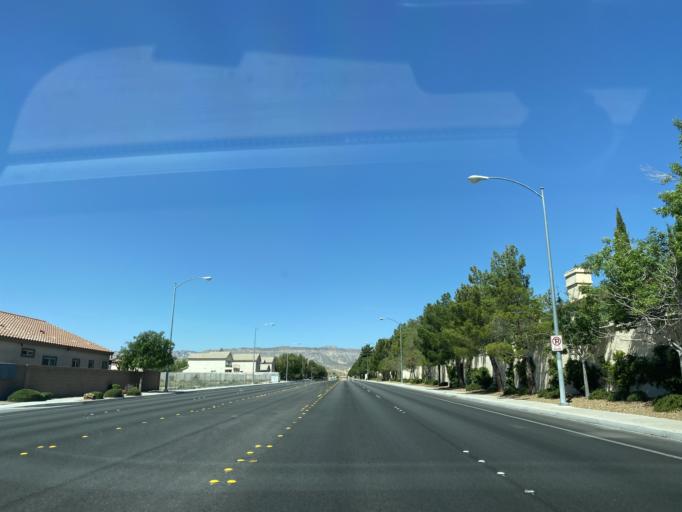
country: US
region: Nevada
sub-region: Clark County
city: Spring Valley
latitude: 36.0924
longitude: -115.2660
